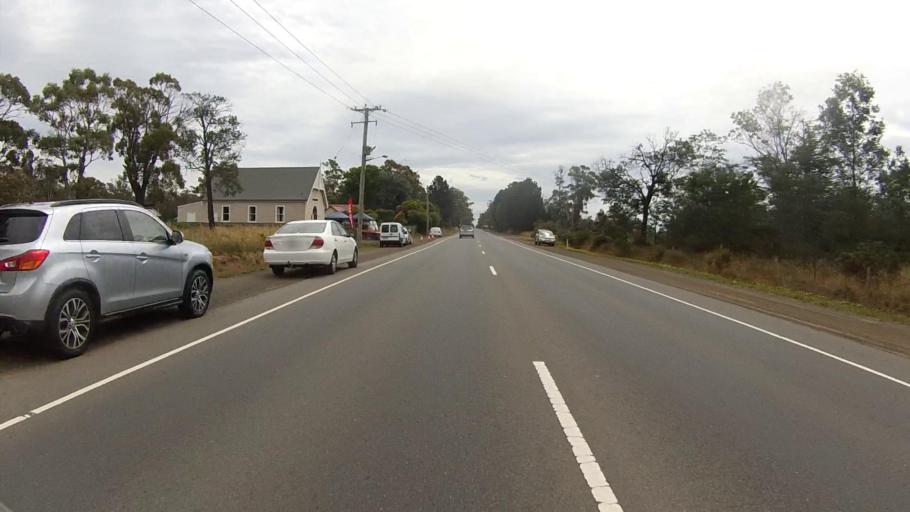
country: AU
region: Tasmania
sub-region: Northern Midlands
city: Evandale
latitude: -41.7587
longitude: 147.3500
